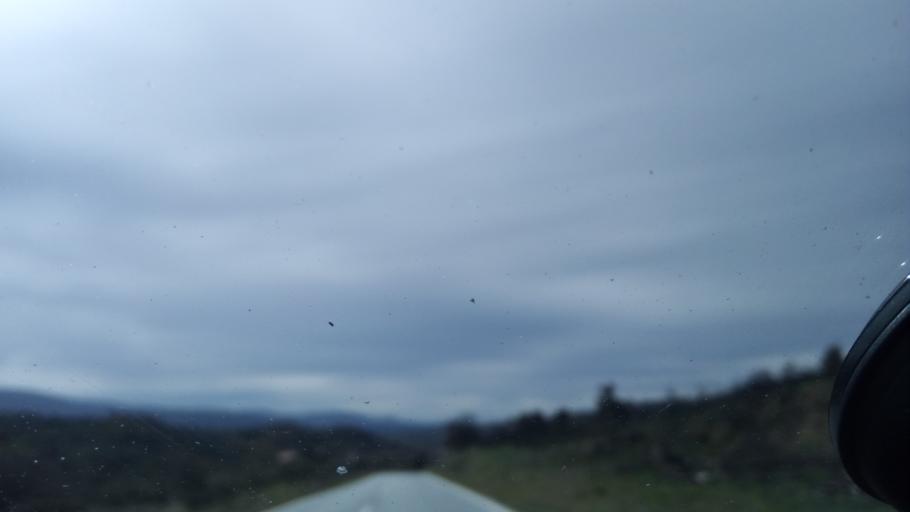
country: PT
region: Guarda
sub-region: Fornos de Algodres
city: Fornos de Algodres
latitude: 40.5721
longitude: -7.5517
